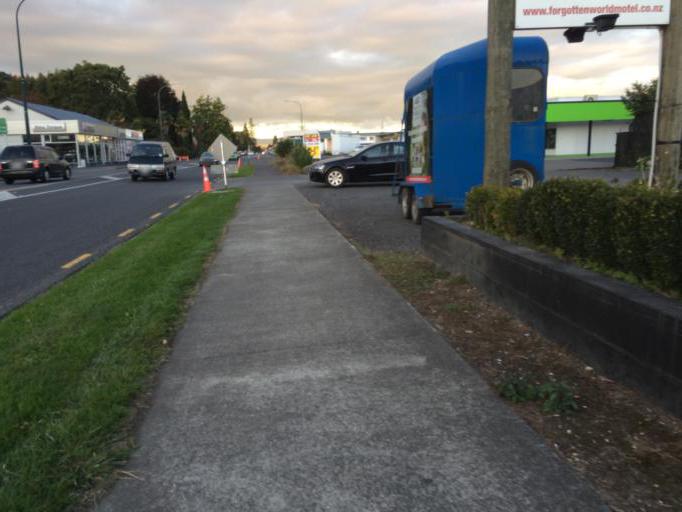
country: NZ
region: Waikato
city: Turangi
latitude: -38.8832
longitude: 175.2576
